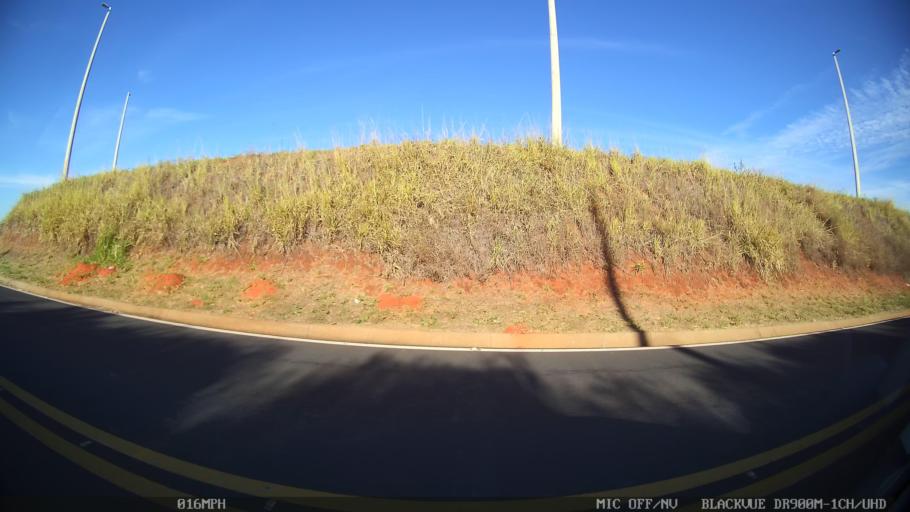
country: BR
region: Sao Paulo
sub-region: Bady Bassitt
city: Bady Bassitt
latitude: -20.8790
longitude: -49.4227
